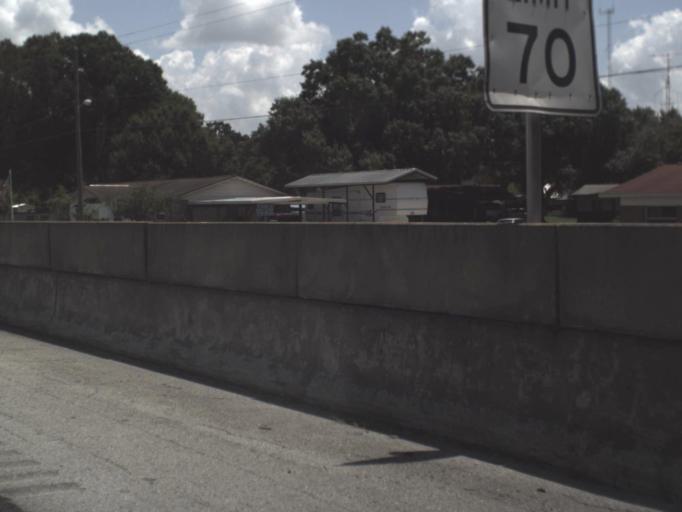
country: US
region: Florida
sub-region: Hillsborough County
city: Plant City
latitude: 28.0366
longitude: -82.1160
